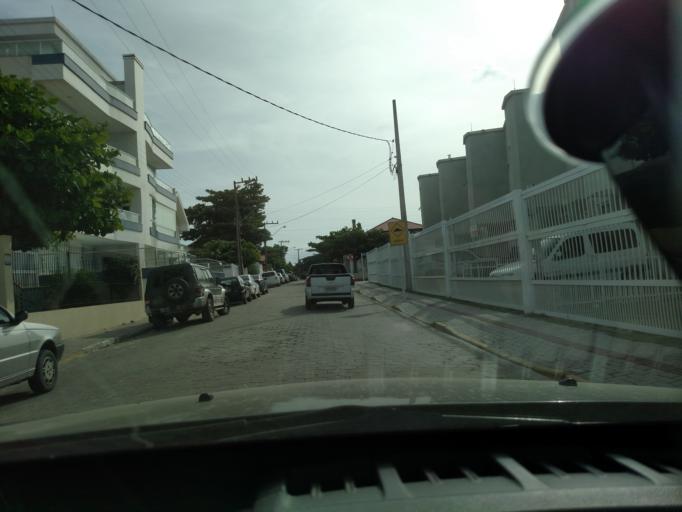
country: BR
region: Santa Catarina
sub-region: Porto Belo
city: Porto Belo
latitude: -27.1978
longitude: -48.4963
